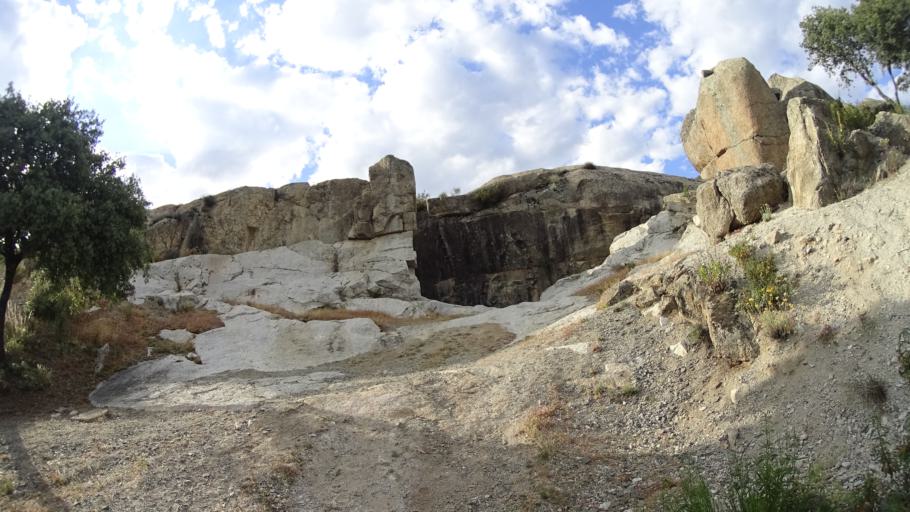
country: ES
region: Madrid
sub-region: Provincia de Madrid
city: Hoyo de Manzanares
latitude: 40.6350
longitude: -3.9023
